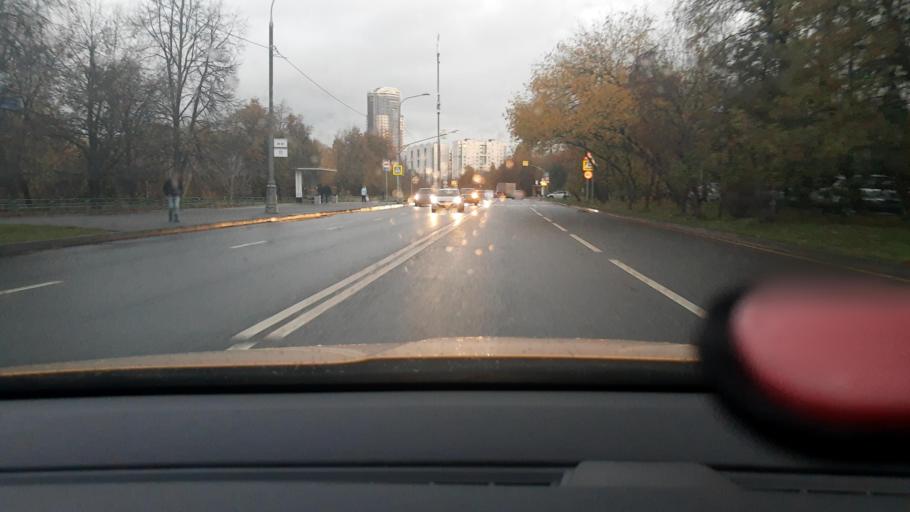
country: RU
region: Moscow
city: Strogino
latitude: 55.8112
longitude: 37.4127
